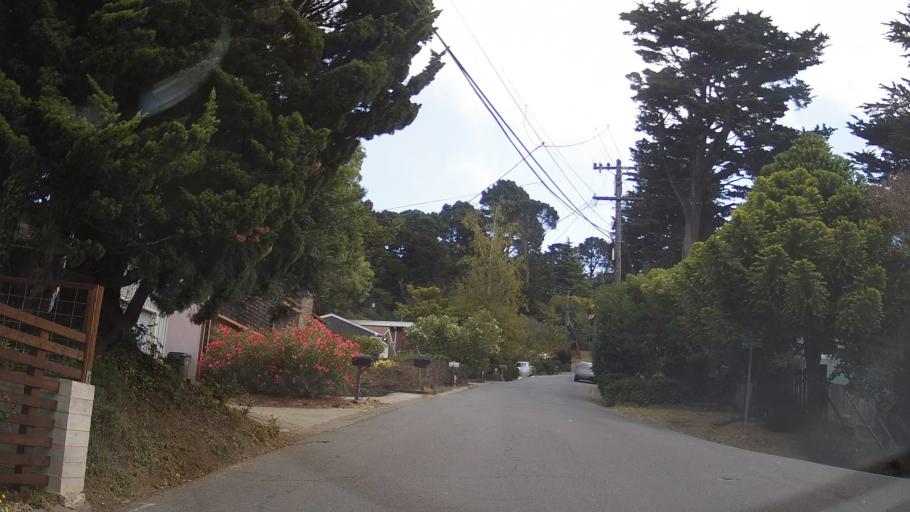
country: US
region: California
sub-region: Contra Costa County
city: Orinda
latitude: 37.8336
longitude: -122.1879
